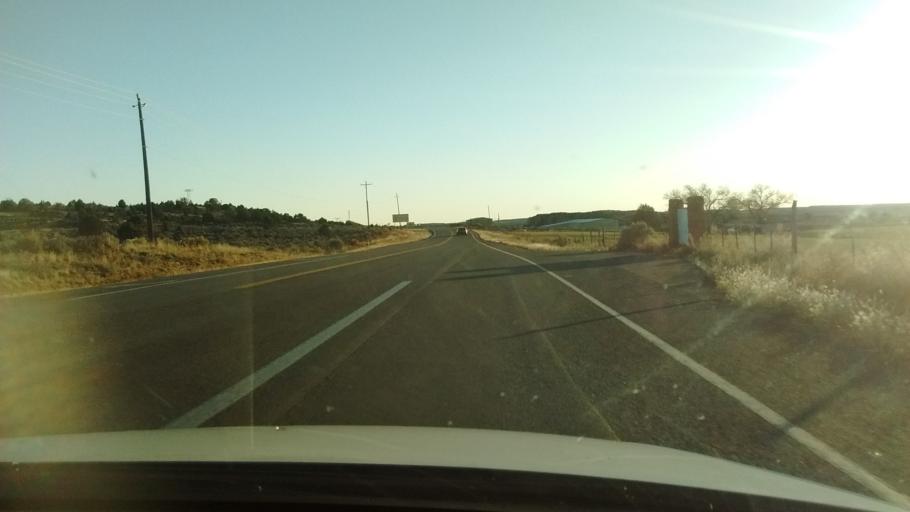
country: US
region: Utah
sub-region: Kane County
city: Kanab
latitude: 37.0064
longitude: -112.5285
